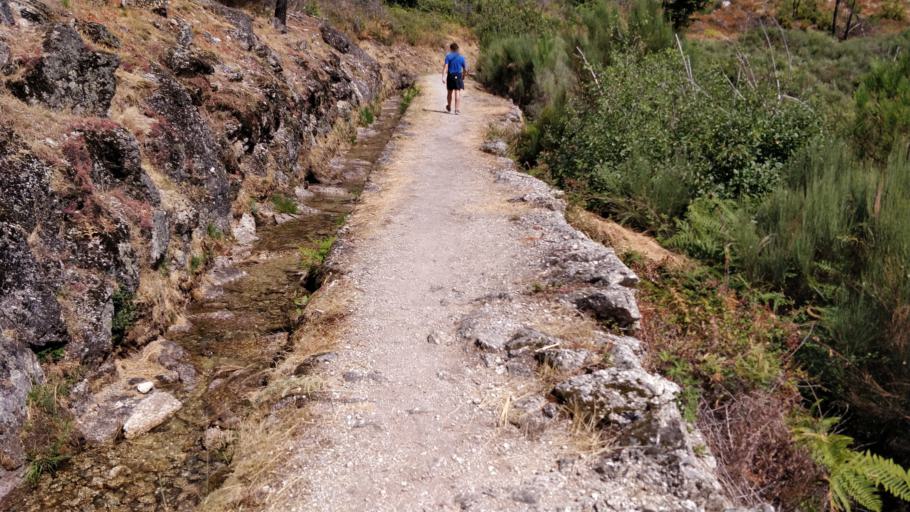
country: PT
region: Guarda
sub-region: Seia
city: Seia
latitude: 40.3862
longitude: -7.6932
